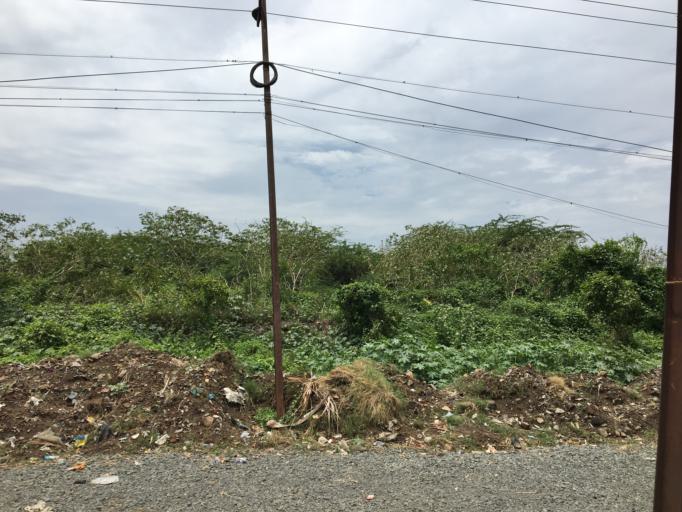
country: IN
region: Tamil Nadu
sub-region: Kancheepuram
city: Madipakkam
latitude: 12.9582
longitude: 80.2139
